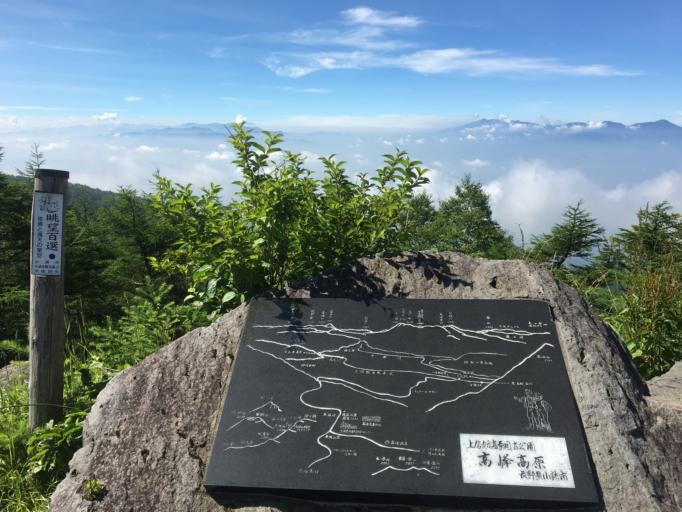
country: JP
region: Nagano
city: Komoro
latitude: 36.4040
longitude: 138.4695
